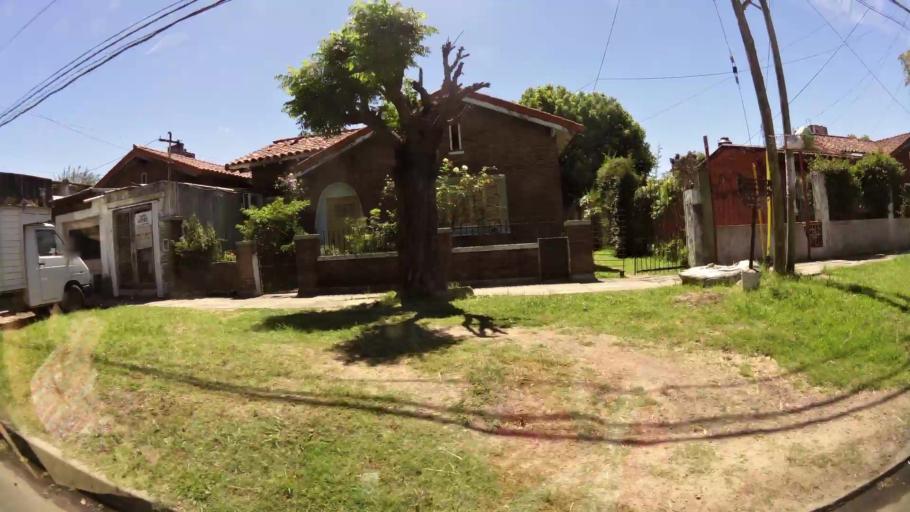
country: AR
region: Buenos Aires
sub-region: Partido de General San Martin
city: General San Martin
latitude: -34.5177
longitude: -58.5558
